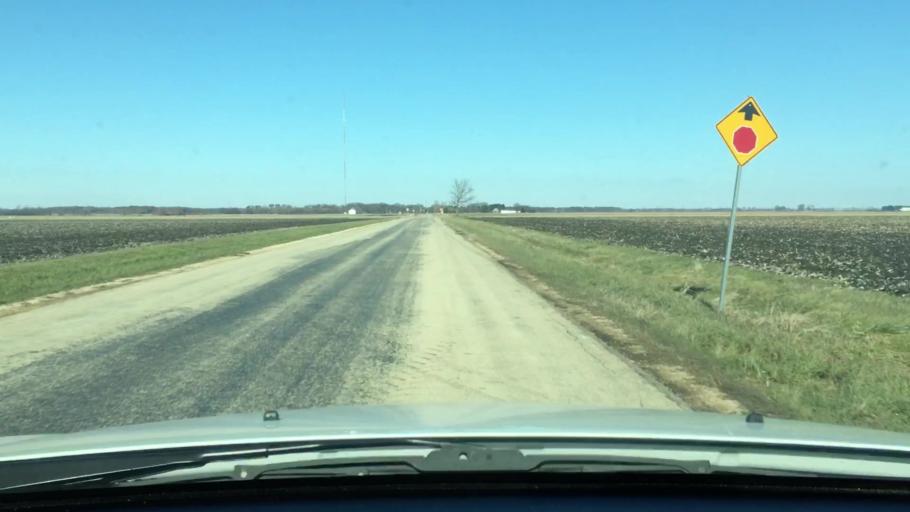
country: US
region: Illinois
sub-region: Ogle County
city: Hillcrest
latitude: 42.0050
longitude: -89.0006
